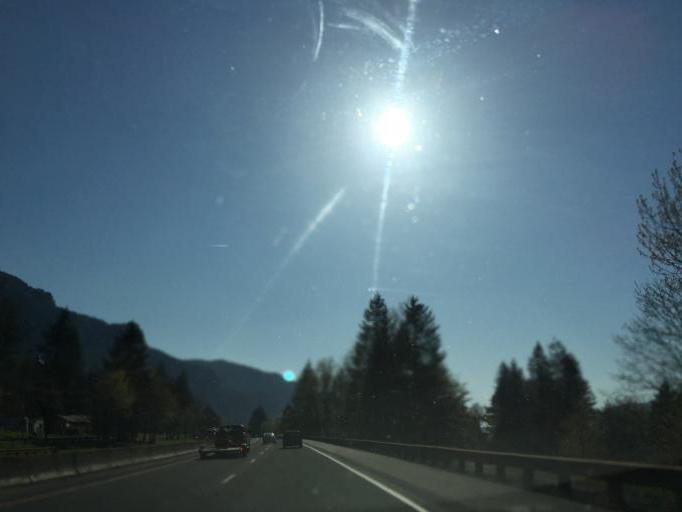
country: US
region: Oregon
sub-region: Hood River County
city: Cascade Locks
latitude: 45.6076
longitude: -122.0339
